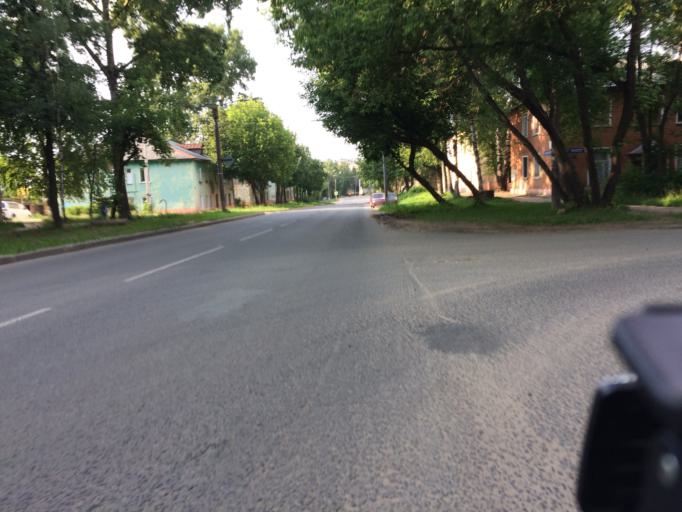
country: RU
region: Mariy-El
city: Yoshkar-Ola
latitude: 56.6271
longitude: 47.9469
